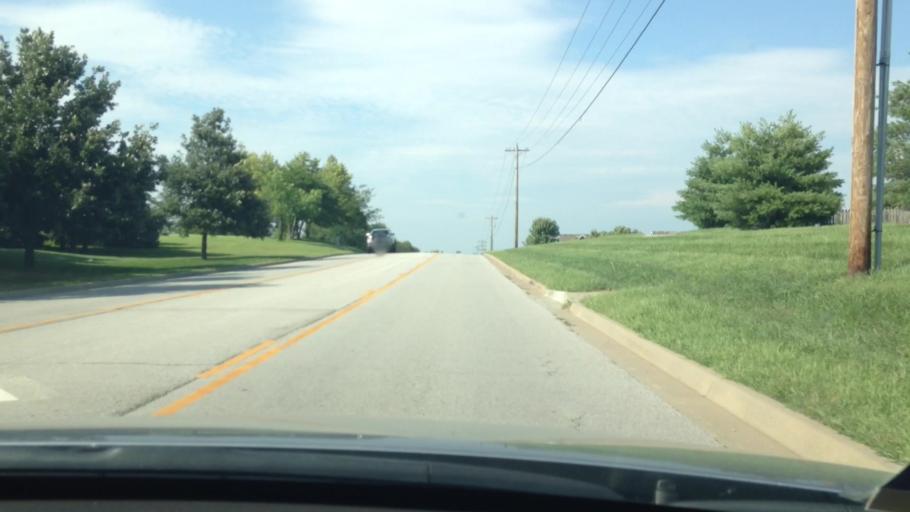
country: US
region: Missouri
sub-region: Platte County
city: Platte City
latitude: 39.3255
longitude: -94.7610
